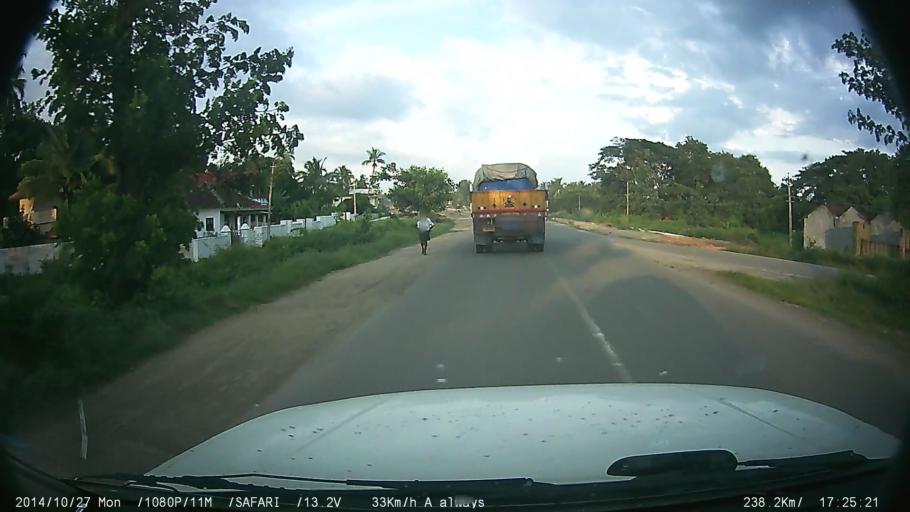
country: IN
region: Kerala
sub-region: Palakkad district
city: Palakkad
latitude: 10.6497
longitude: 76.5641
